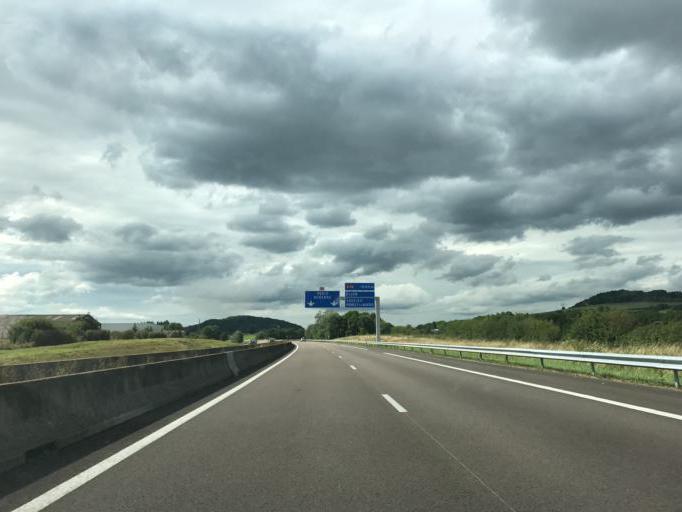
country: FR
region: Bourgogne
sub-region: Departement de la Cote-d'Or
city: Pouilly-en-Auxois
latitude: 47.2455
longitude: 4.5738
